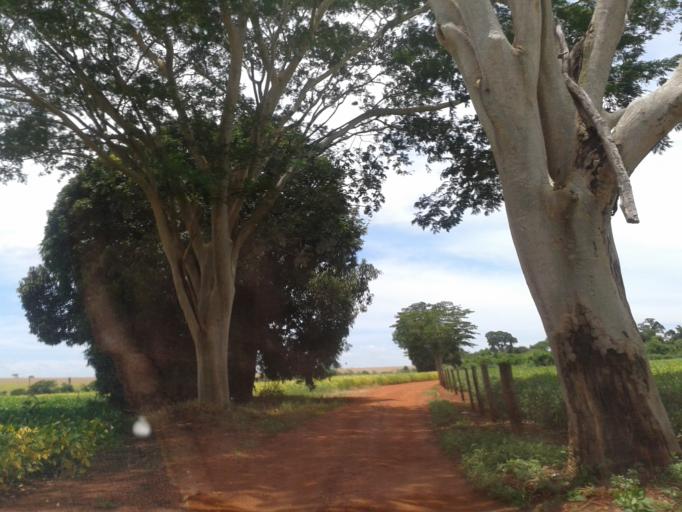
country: BR
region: Minas Gerais
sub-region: Capinopolis
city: Capinopolis
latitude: -18.6557
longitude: -49.7398
